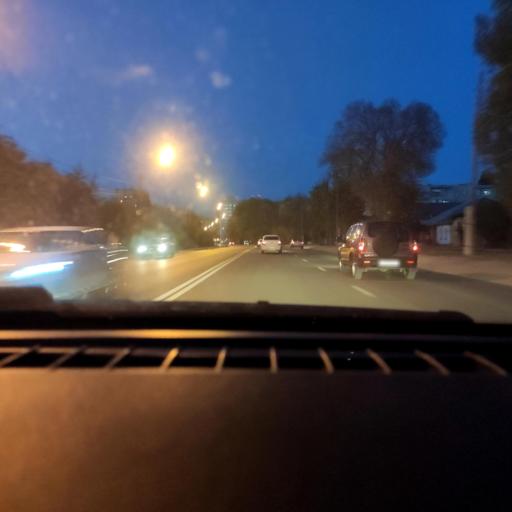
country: RU
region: Voronezj
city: Voronezh
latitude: 51.6577
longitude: 39.2757
